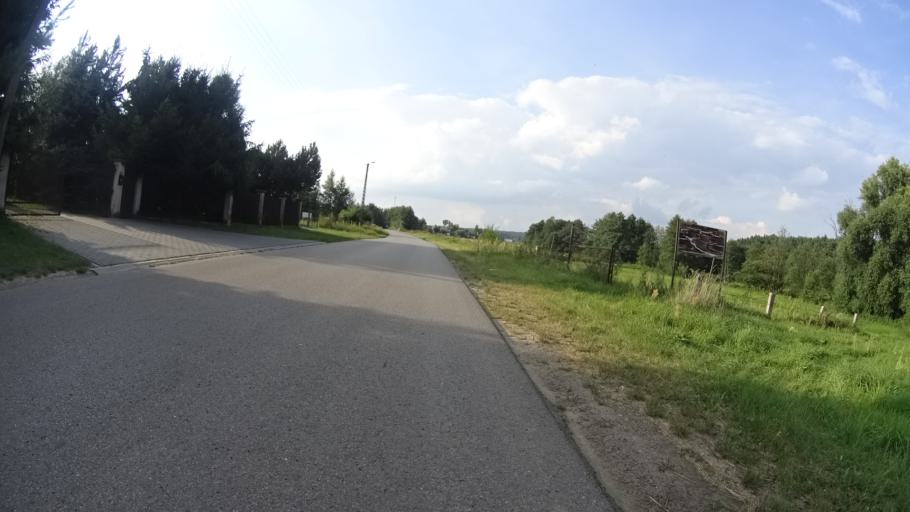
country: PL
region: Masovian Voivodeship
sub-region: Powiat grojecki
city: Mogielnica
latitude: 51.6797
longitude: 20.7335
